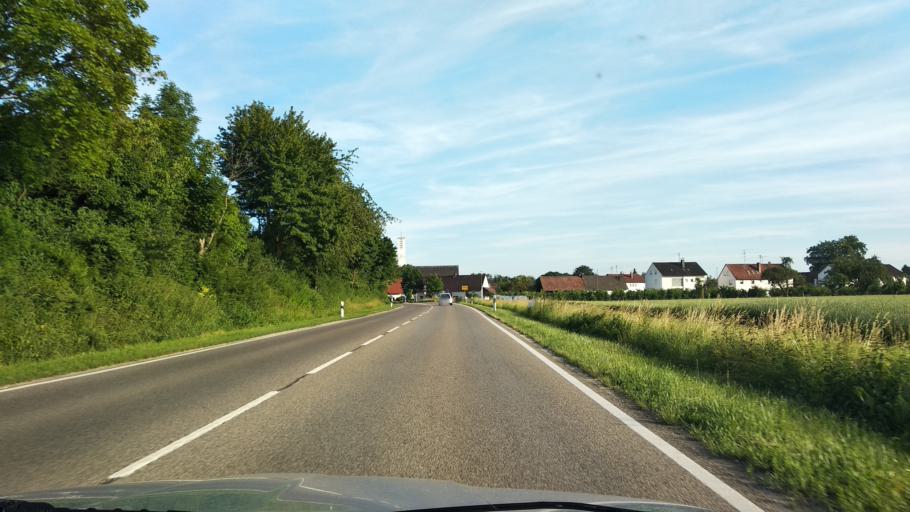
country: DE
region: Bavaria
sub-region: Swabia
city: Bellenberg
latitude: 48.2625
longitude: 10.0904
